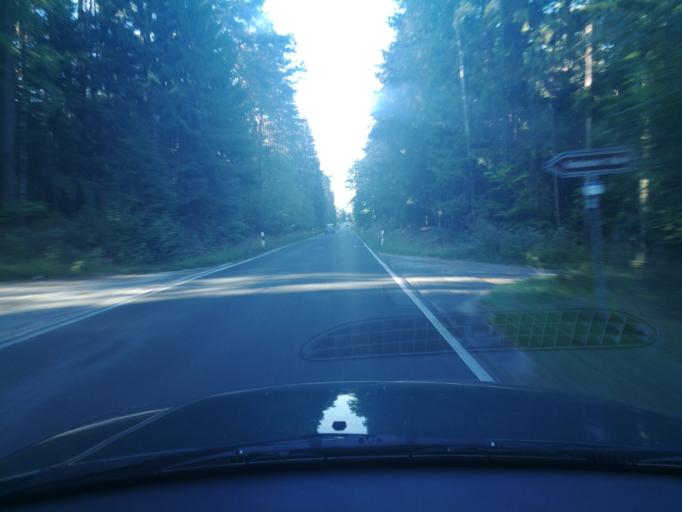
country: DE
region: Bavaria
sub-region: Regierungsbezirk Mittelfranken
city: Hessdorf
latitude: 49.6107
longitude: 10.9379
